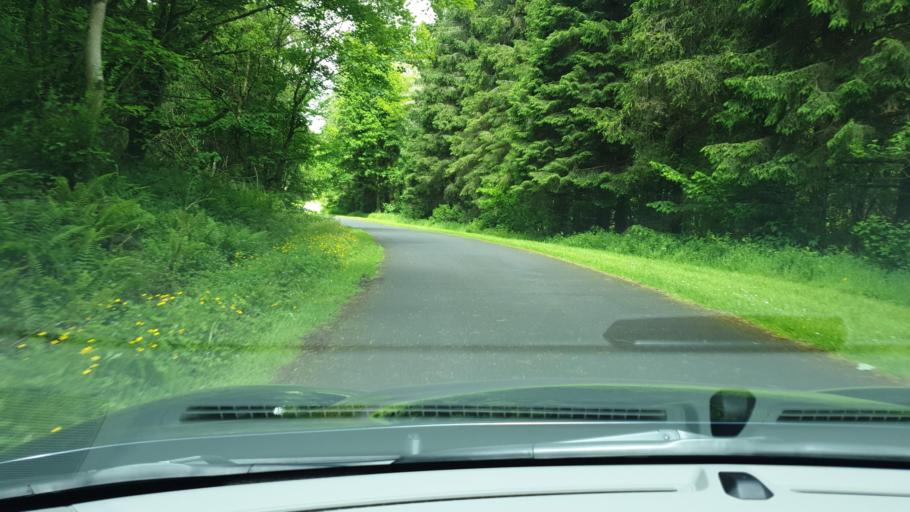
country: IE
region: Ulster
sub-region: An Cabhan
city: Kingscourt
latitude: 53.9144
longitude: -6.7888
